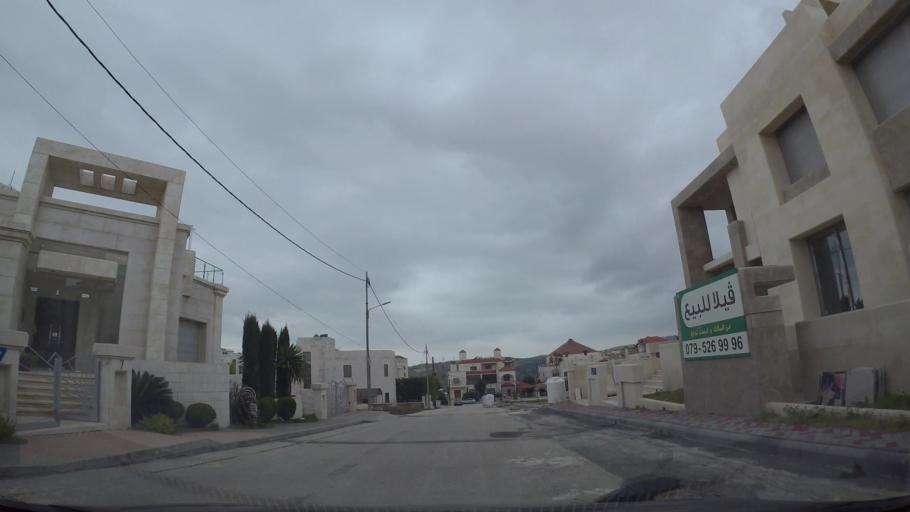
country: JO
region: Amman
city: Wadi as Sir
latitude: 31.9610
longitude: 35.8242
